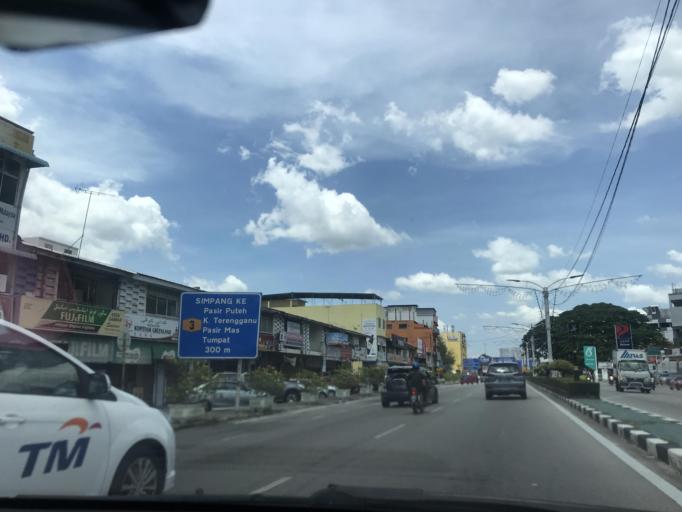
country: MY
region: Kelantan
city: Kota Bharu
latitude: 6.1200
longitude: 102.2408
